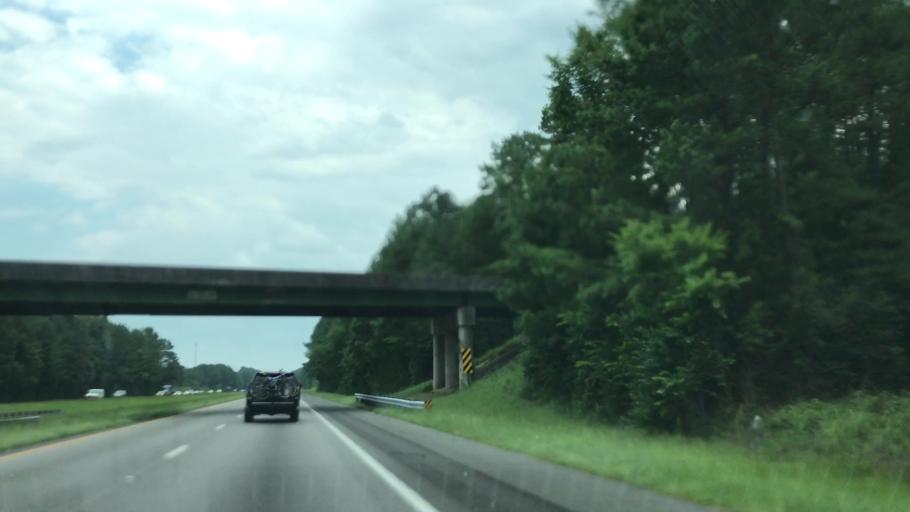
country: US
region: South Carolina
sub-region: Richland County
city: Blythewood
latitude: 34.2829
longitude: -80.9975
